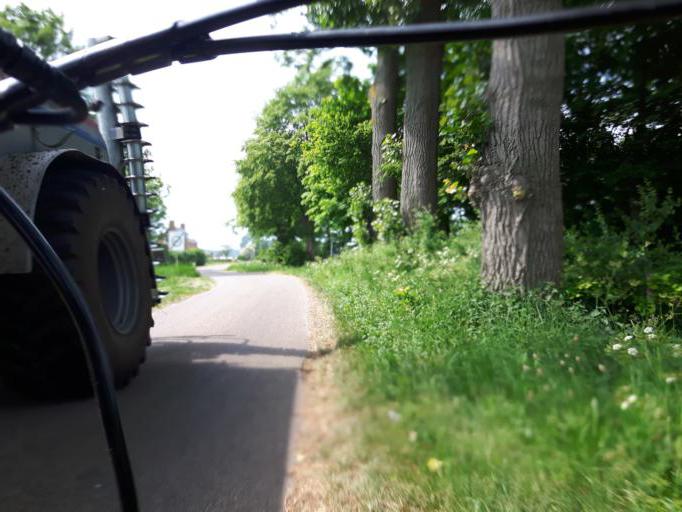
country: NL
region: North Brabant
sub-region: Gemeente Steenbergen
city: Welberg
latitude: 51.5378
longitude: 4.3217
